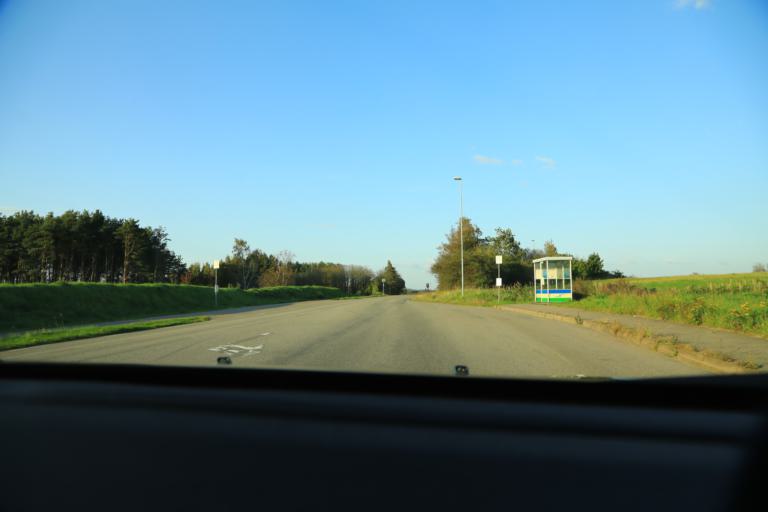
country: SE
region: Halland
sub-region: Varbergs Kommun
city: Traslovslage
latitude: 57.0708
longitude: 12.2873
